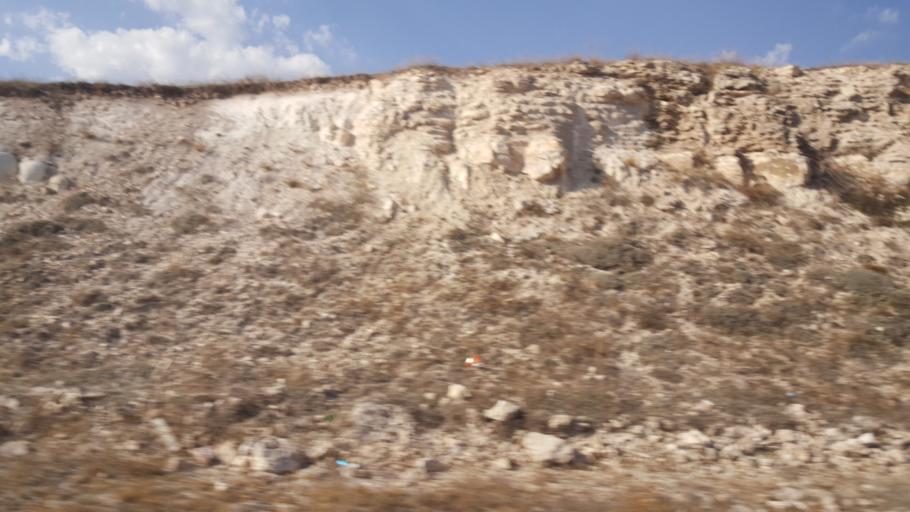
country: TR
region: Eskisehir
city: Kirka
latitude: 39.3162
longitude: 30.5474
